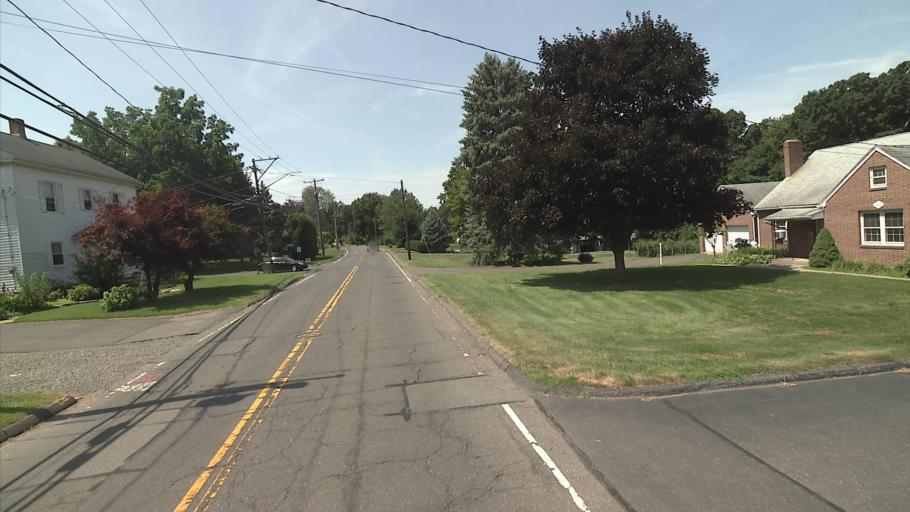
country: US
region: Connecticut
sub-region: Hartford County
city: Kensington
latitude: 41.6224
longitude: -72.7835
